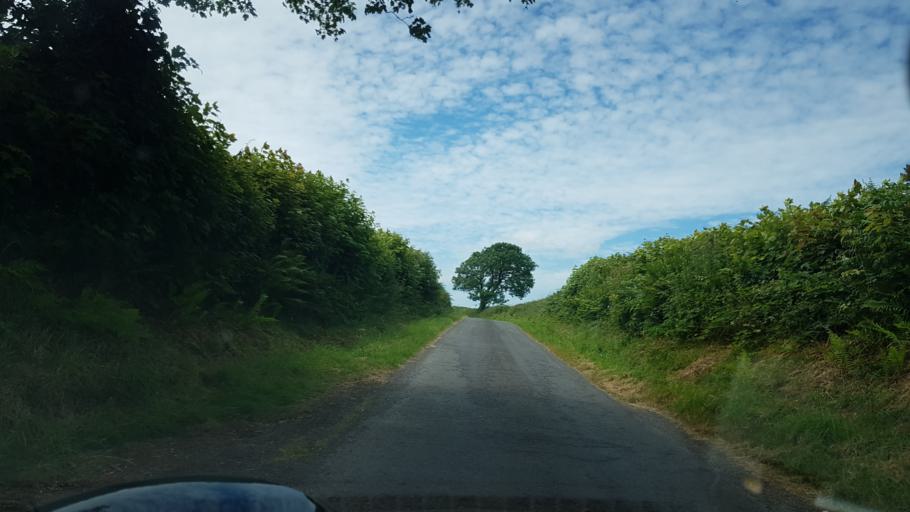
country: GB
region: Wales
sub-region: Carmarthenshire
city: Llanddowror
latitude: 51.7677
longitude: -4.5032
